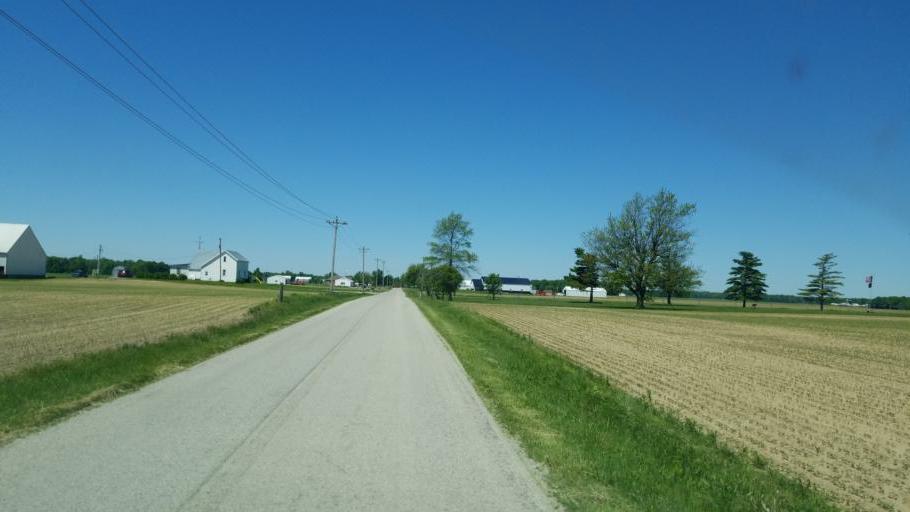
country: US
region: Ohio
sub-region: Shelby County
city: Anna
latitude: 40.3723
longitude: -84.2697
